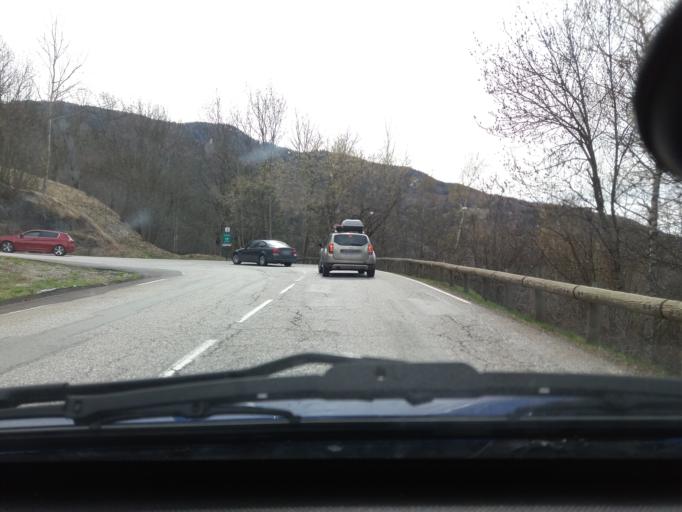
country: FR
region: Rhone-Alpes
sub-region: Departement de la Savoie
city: Macot-la-Plagne
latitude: 45.5445
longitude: 6.6682
